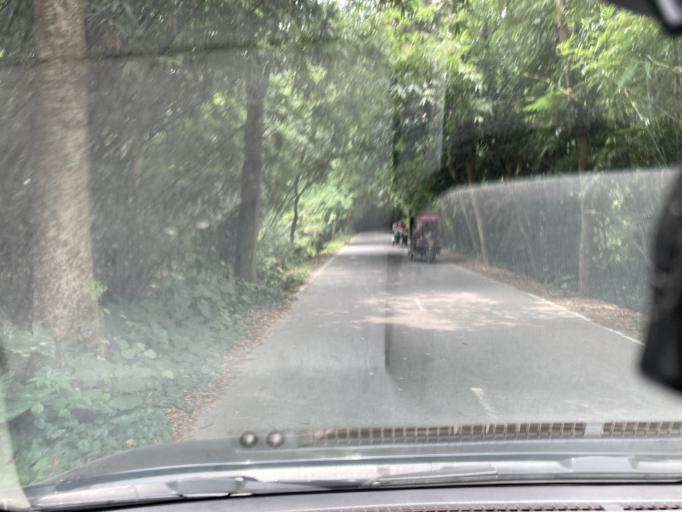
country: BD
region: Dhaka
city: Dohar
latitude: 23.7916
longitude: 90.0585
